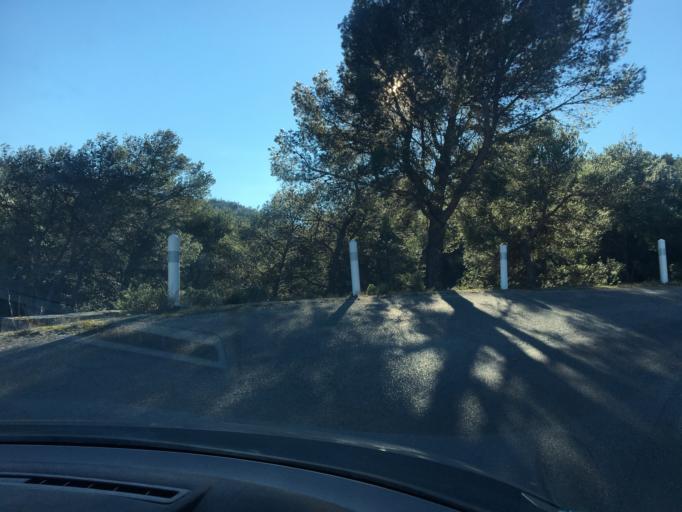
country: FR
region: Provence-Alpes-Cote d'Azur
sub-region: Departement des Bouches-du-Rhone
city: Maussane-les-Alpilles
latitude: 43.7579
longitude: 4.7940
